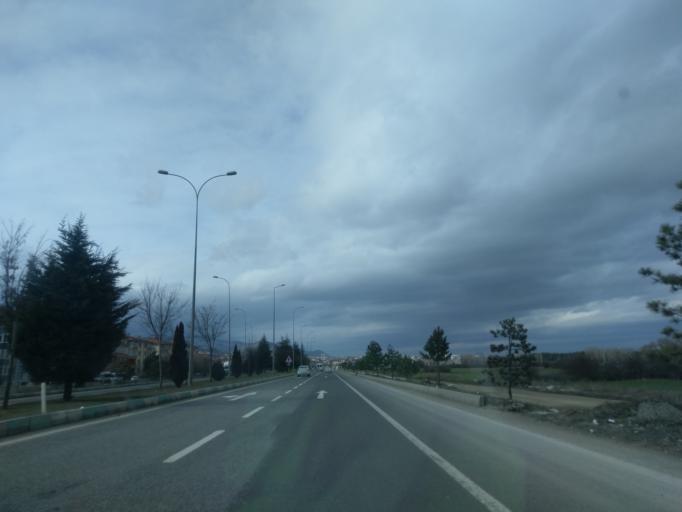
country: TR
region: Kuetahya
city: Kutahya
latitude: 39.4115
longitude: 30.0170
